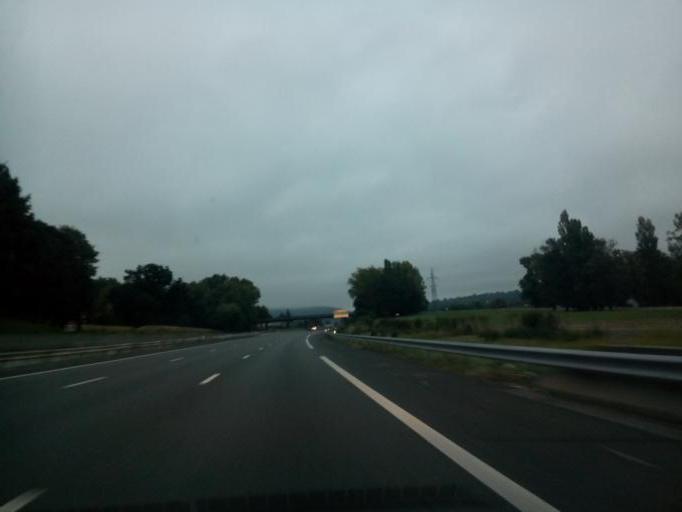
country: FR
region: Rhone-Alpes
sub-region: Departement de l'Isere
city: Bourgoin
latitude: 45.5936
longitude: 5.2908
